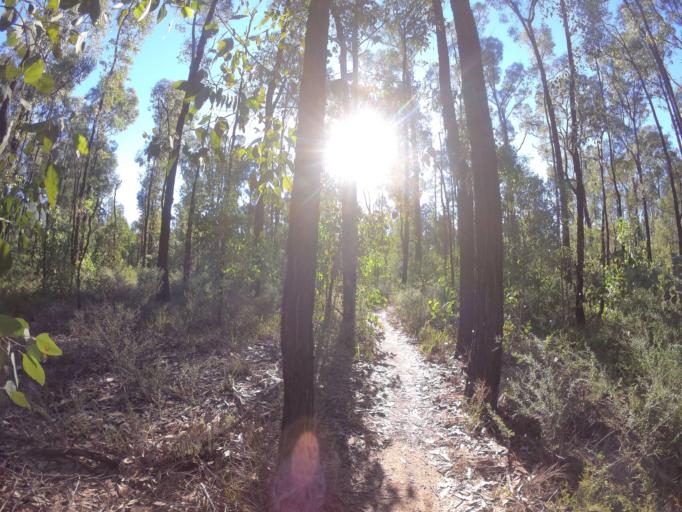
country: AU
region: New South Wales
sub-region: Hawkesbury
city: South Windsor
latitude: -33.6431
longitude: 150.7921
